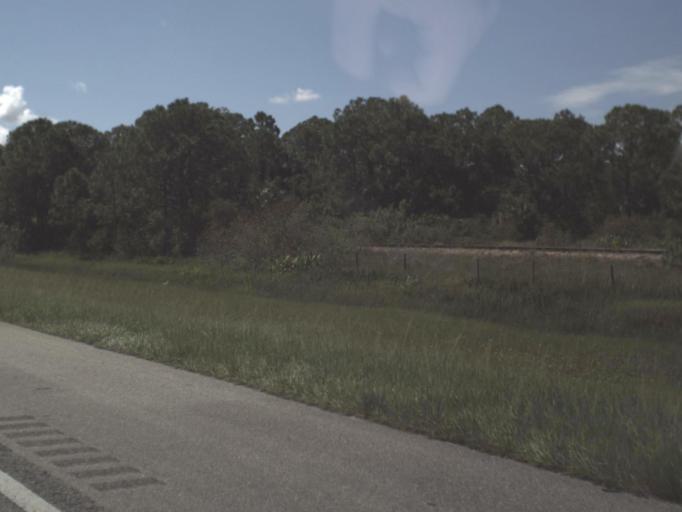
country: US
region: Florida
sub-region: Lee County
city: Suncoast Estates
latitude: 26.8126
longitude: -81.9344
